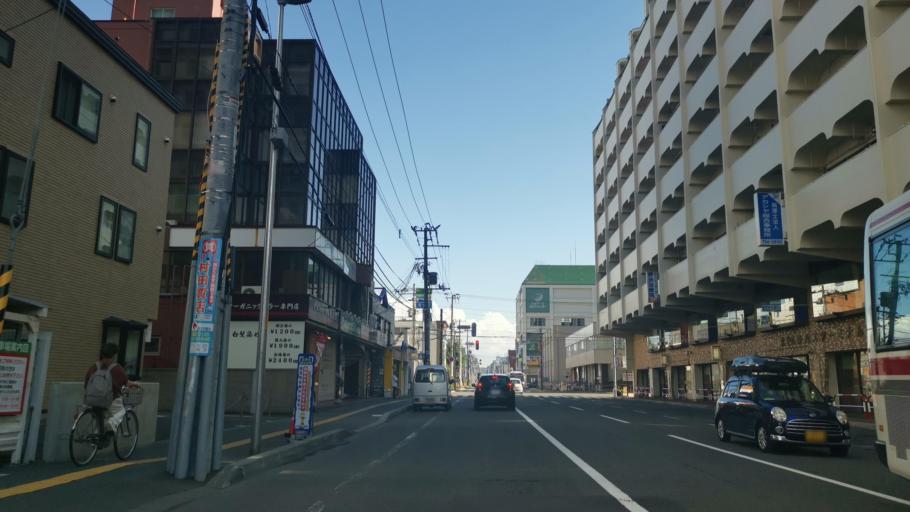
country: JP
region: Hokkaido
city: Sapporo
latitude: 43.0901
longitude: 141.3447
